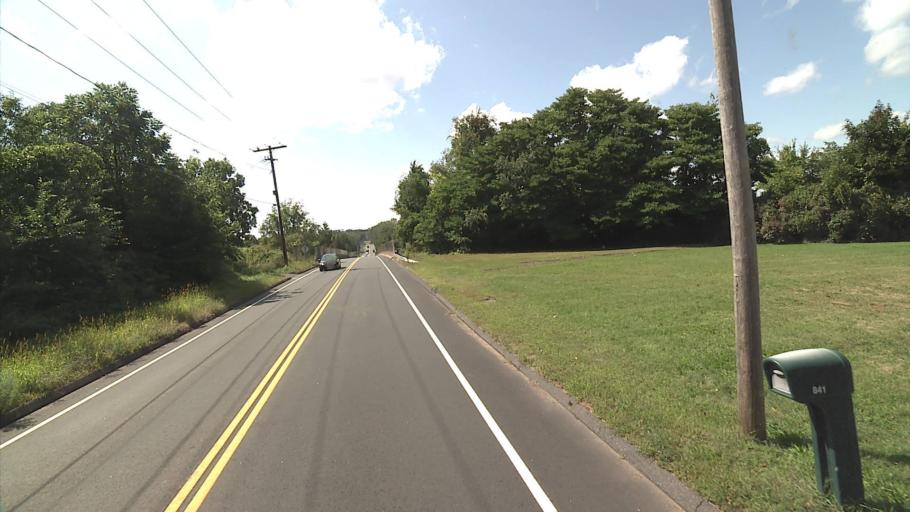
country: US
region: Connecticut
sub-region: Hartford County
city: Wethersfield
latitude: 41.6594
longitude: -72.6686
